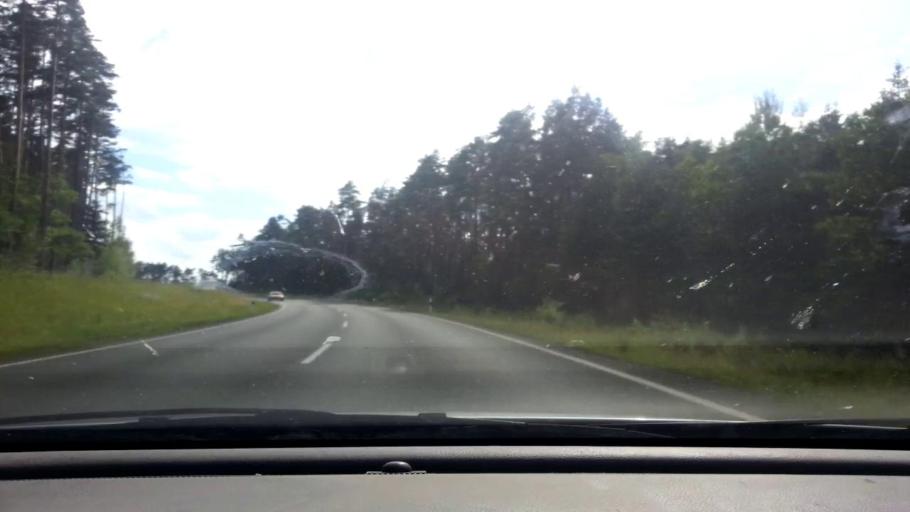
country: DE
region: Bavaria
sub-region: Upper Franconia
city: Neunkirchen am Main
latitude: 49.9241
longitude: 11.6228
